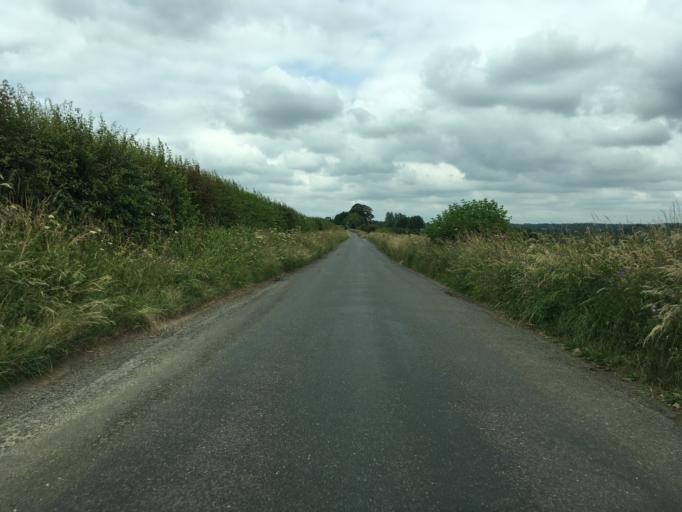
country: GB
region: England
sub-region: Oxfordshire
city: Charlbury
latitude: 51.9172
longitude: -1.4774
